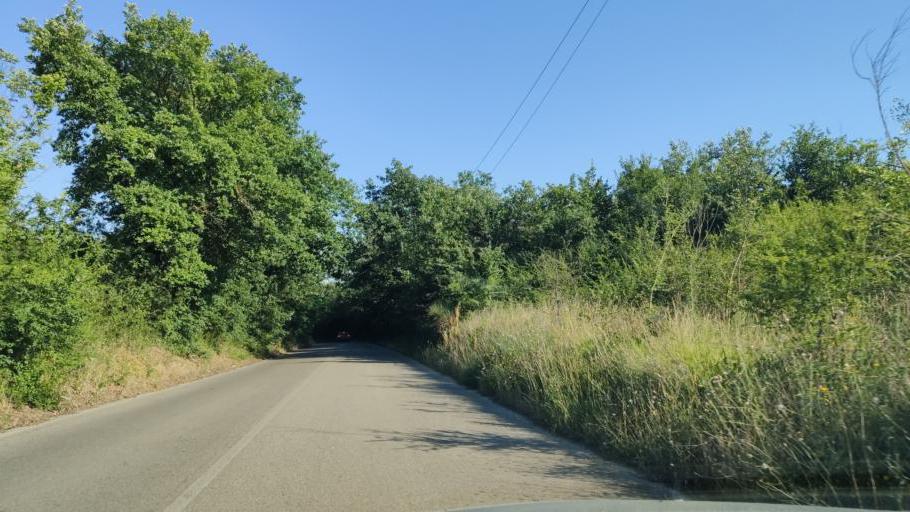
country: IT
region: Latium
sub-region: Provincia di Viterbo
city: Orte
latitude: 42.4715
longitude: 12.3697
